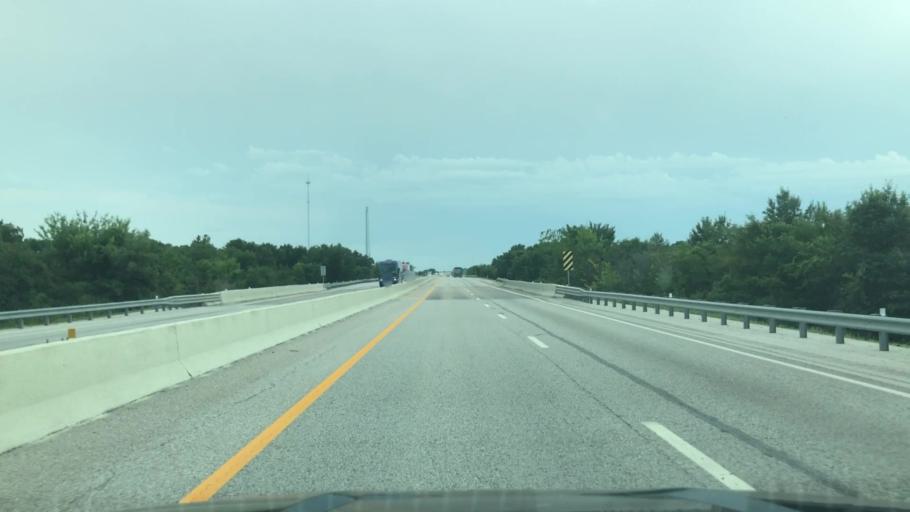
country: US
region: Oklahoma
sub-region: Craig County
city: Vinita
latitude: 36.5866
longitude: -95.2003
